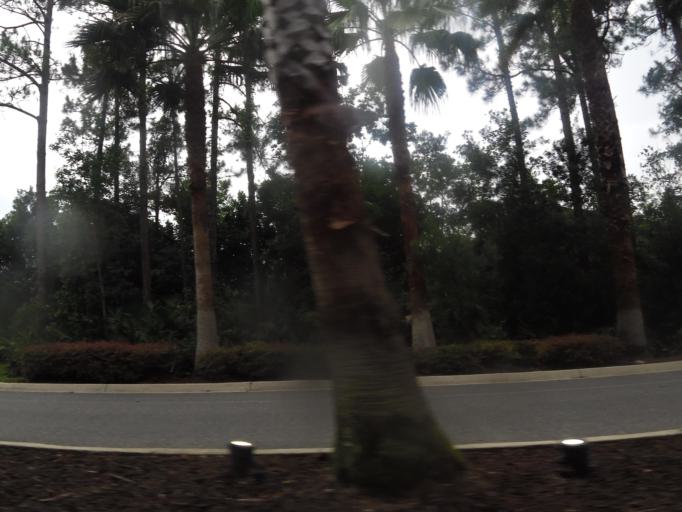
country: US
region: Florida
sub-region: Duval County
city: Jacksonville Beach
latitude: 30.2604
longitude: -81.4542
